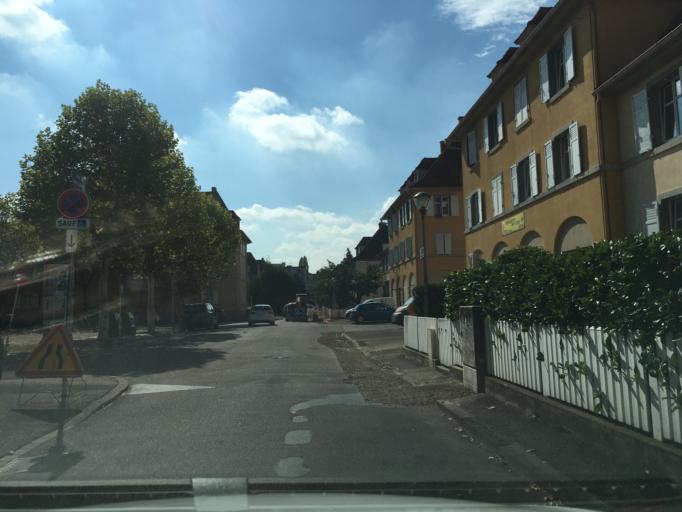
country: FR
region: Alsace
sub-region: Departement du Haut-Rhin
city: Colmar
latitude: 48.0733
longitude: 7.3349
